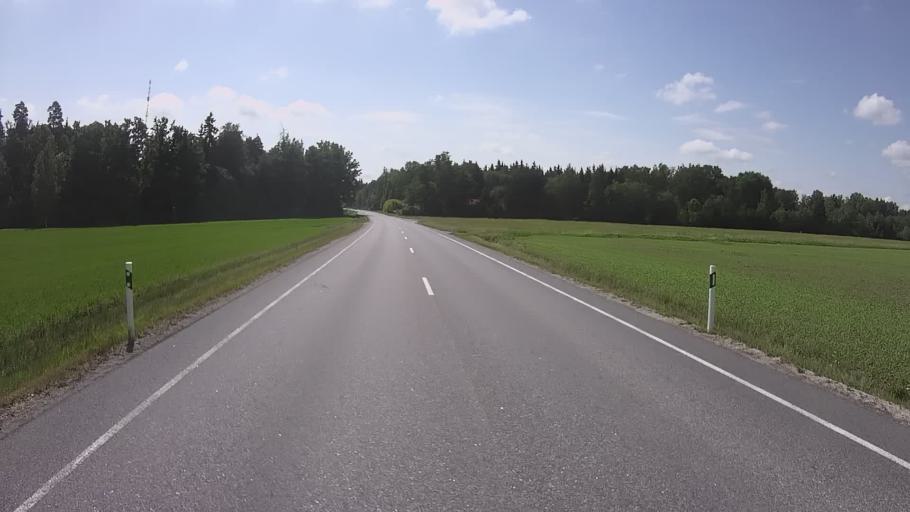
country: EE
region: Tartu
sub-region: Tartu linn
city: Tartu
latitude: 58.3748
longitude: 26.8839
